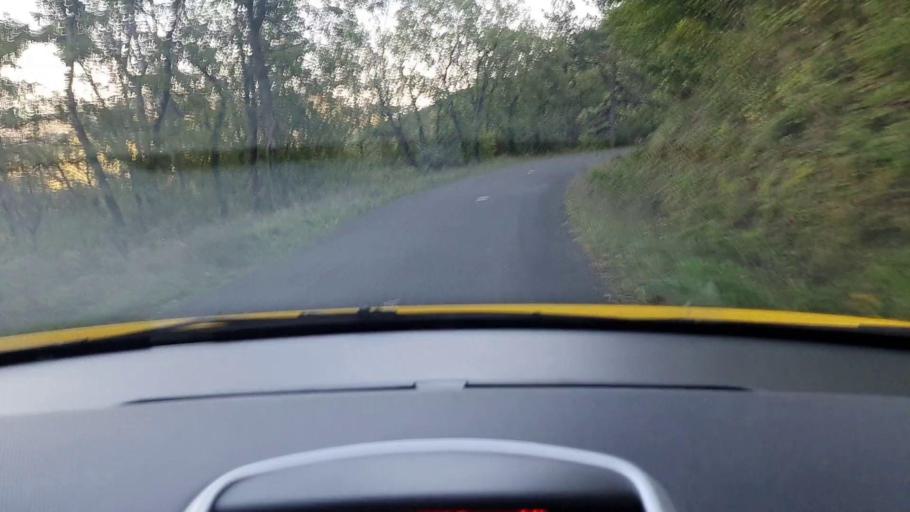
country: FR
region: Languedoc-Roussillon
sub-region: Departement du Gard
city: Saint-Hippolyte-du-Fort
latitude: 43.9705
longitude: 3.7938
